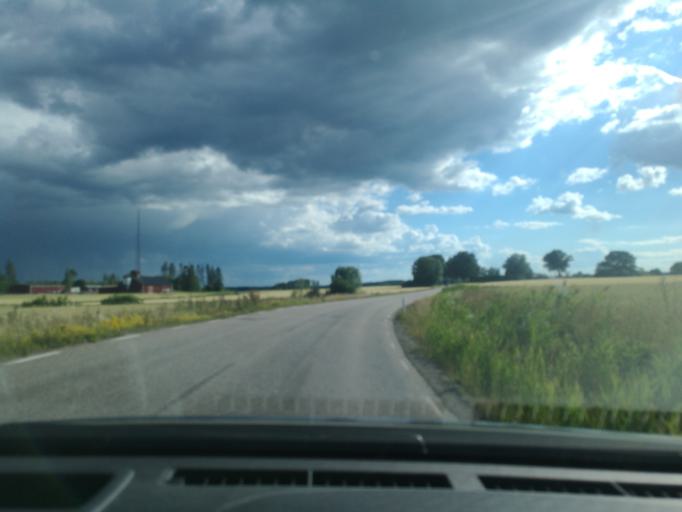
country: SE
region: Soedermanland
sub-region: Eskilstuna Kommun
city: Arla
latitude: 59.4406
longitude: 16.7177
